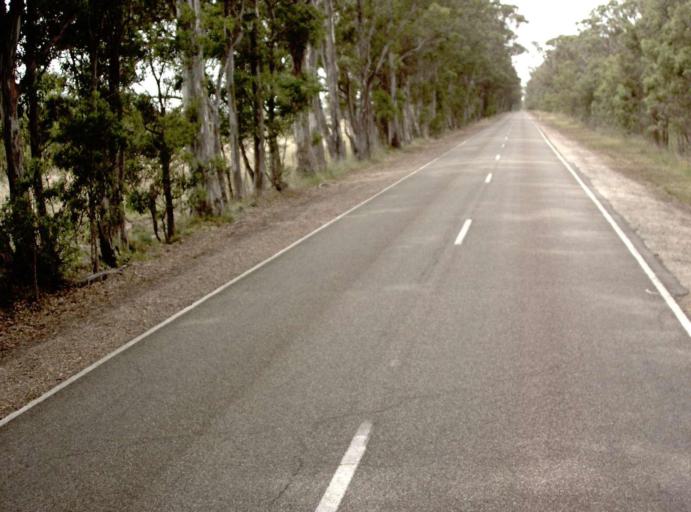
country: AU
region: Victoria
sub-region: Wellington
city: Sale
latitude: -37.8923
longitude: 147.0684
